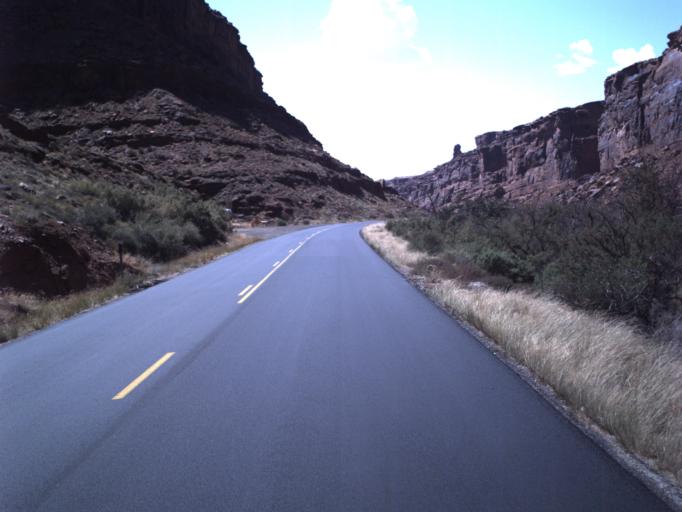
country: US
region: Utah
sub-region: Grand County
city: Moab
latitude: 38.6275
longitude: -109.5044
